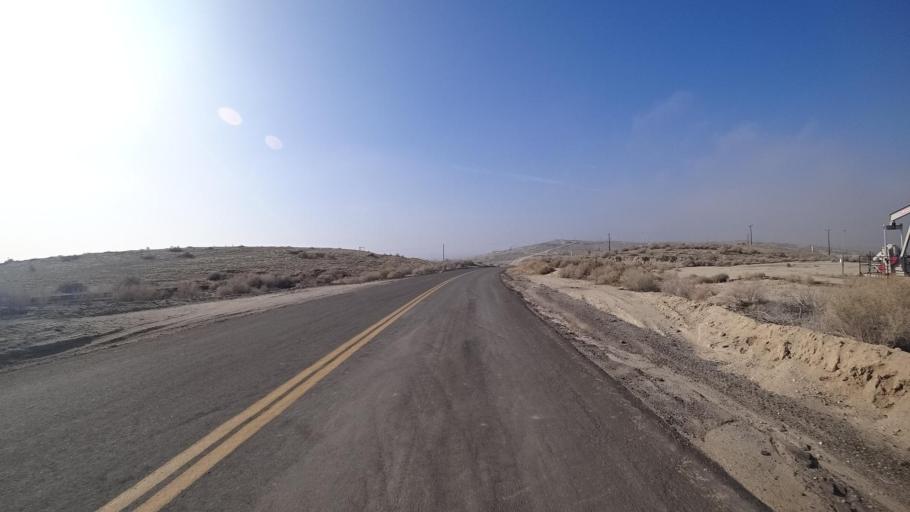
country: US
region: California
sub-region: Kern County
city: Ford City
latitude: 35.1631
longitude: -119.4177
